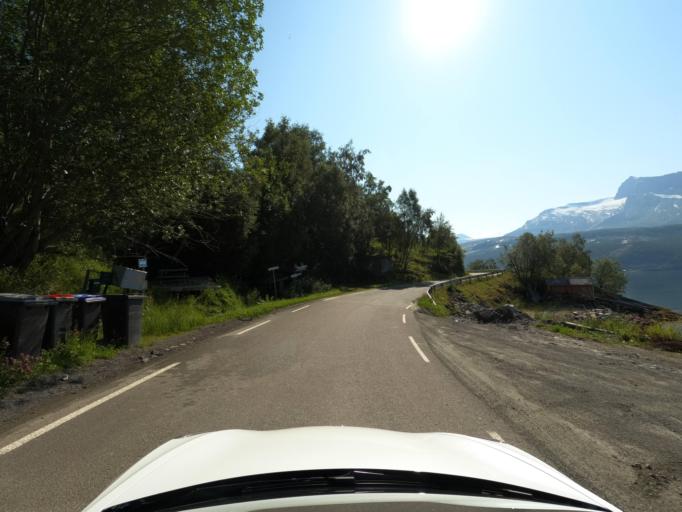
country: NO
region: Nordland
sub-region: Narvik
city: Narvik
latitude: 68.2956
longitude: 17.3568
